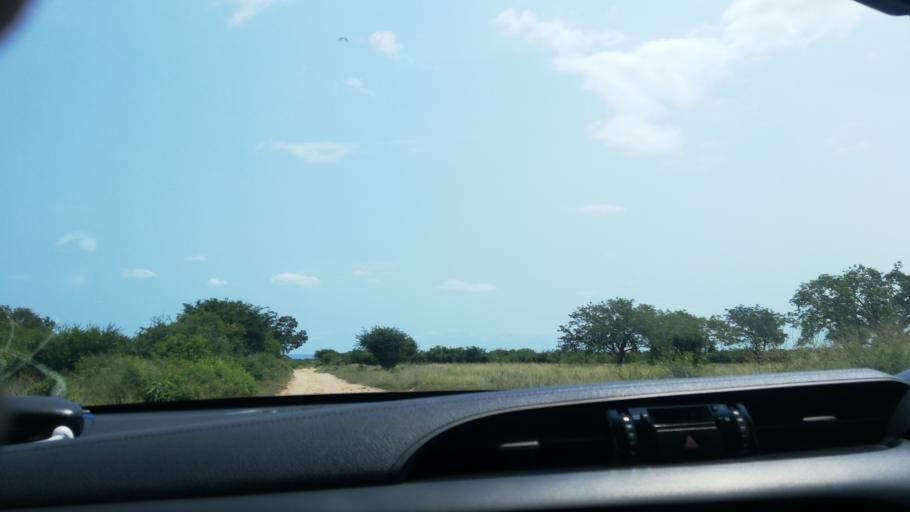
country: MZ
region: Maputo
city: Matola
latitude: -26.1101
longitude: 32.4135
